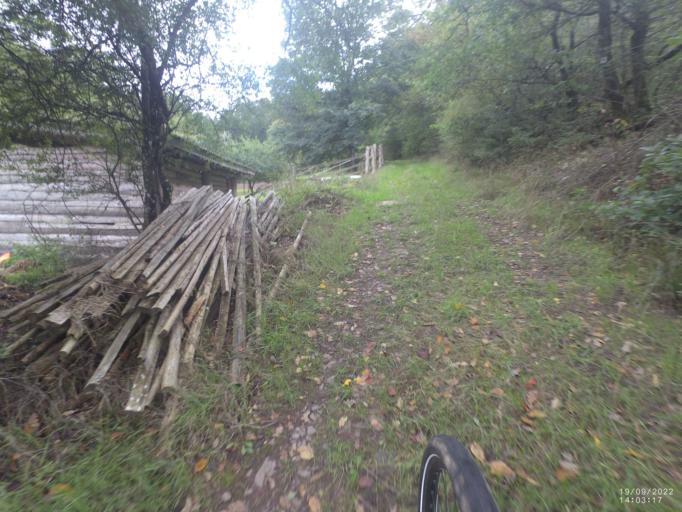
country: DE
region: Rheinland-Pfalz
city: Schutz
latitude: 50.1259
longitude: 6.7599
